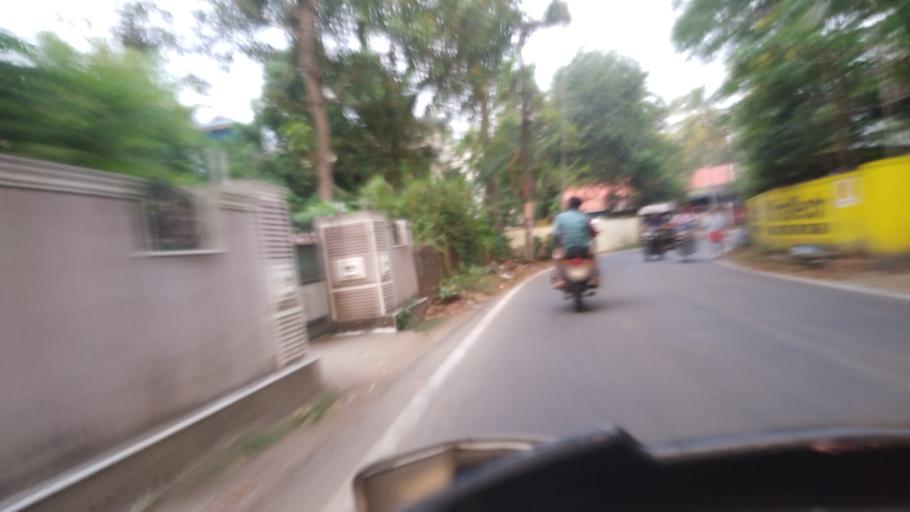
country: IN
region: Kerala
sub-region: Thrissur District
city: Kodungallur
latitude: 10.1654
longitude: 76.2045
